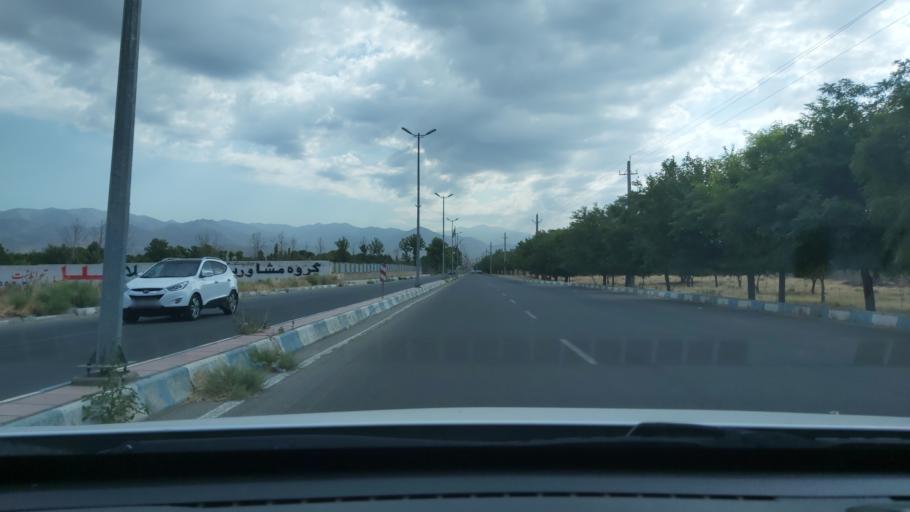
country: IR
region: Alborz
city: Hashtgerd
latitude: 35.9395
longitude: 50.7659
